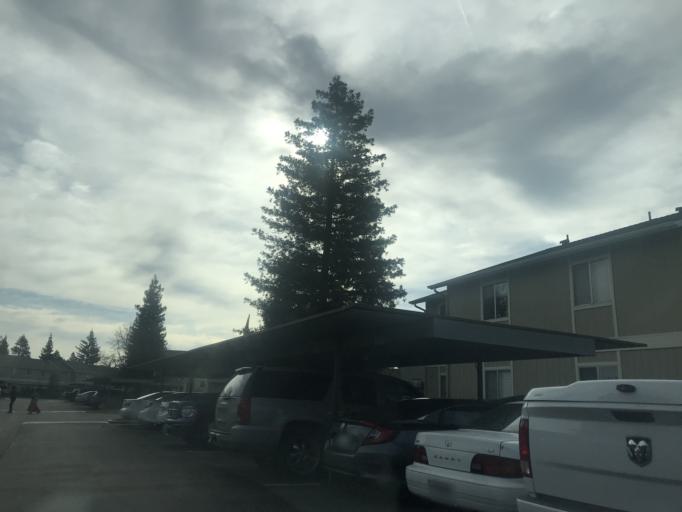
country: US
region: California
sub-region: Yolo County
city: Woodland
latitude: 38.6660
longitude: -121.7583
